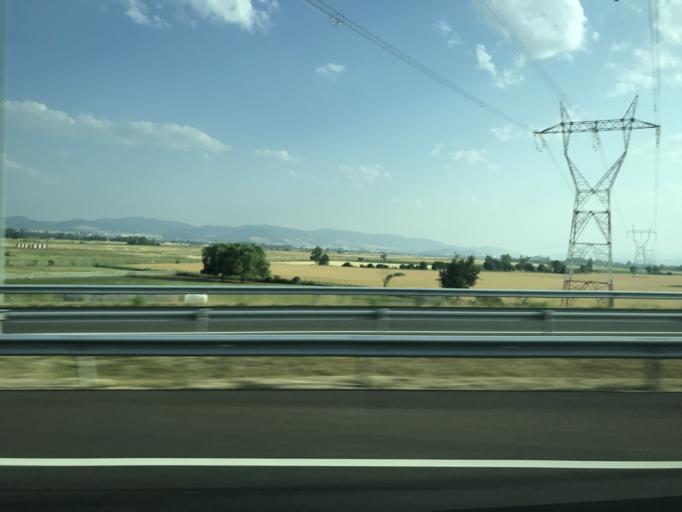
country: ES
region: Basque Country
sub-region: Provincia de Alava
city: Gasteiz / Vitoria
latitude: 42.9021
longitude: -2.7116
